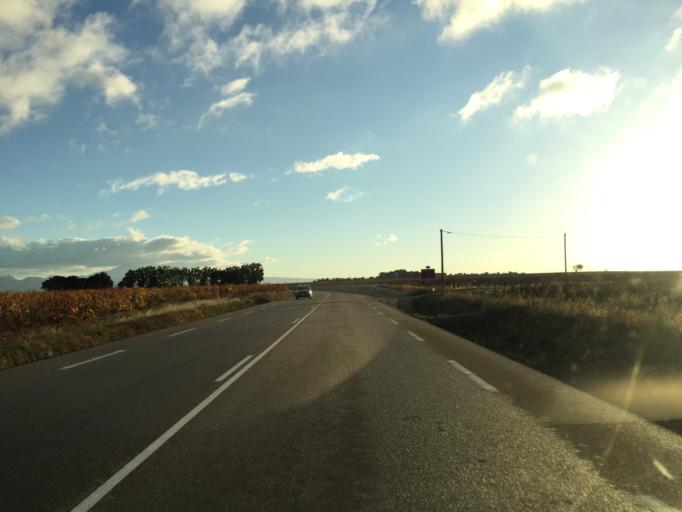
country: FR
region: Provence-Alpes-Cote d'Azur
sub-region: Departement du Vaucluse
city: Chateauneuf-du-Pape
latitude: 44.0958
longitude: 4.8345
